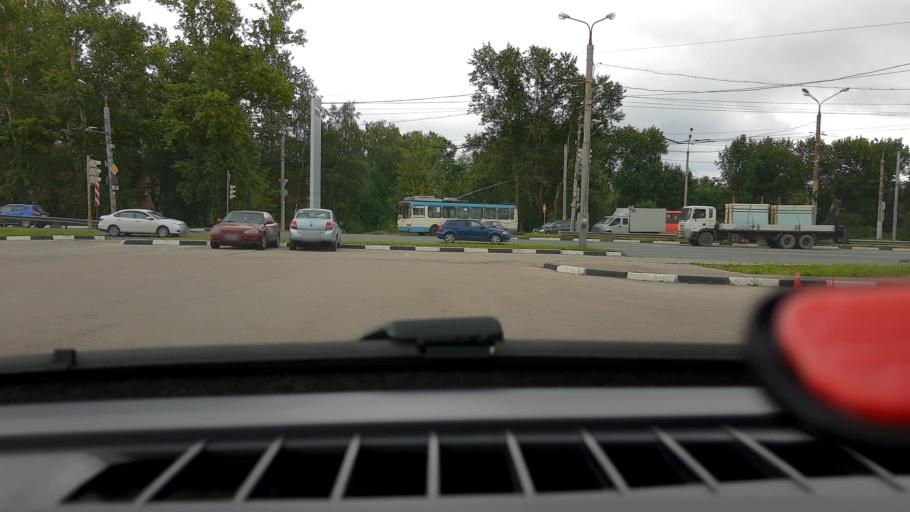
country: RU
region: Nizjnij Novgorod
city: Gorbatovka
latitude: 56.3113
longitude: 43.8006
